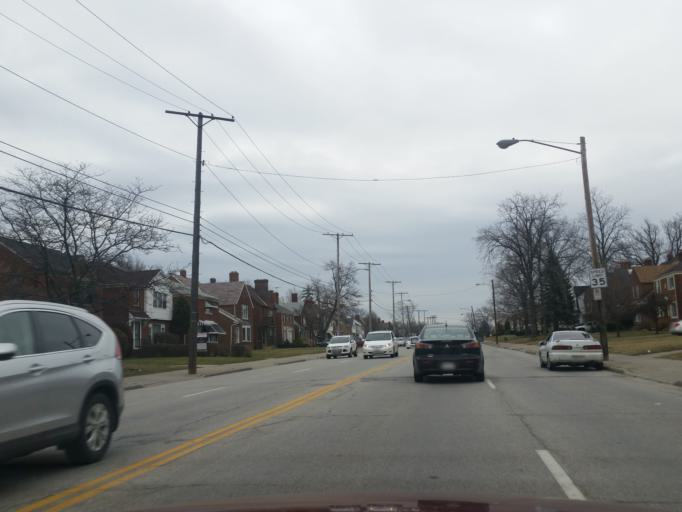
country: US
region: Ohio
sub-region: Cuyahoga County
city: University Heights
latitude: 41.5013
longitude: -81.5540
